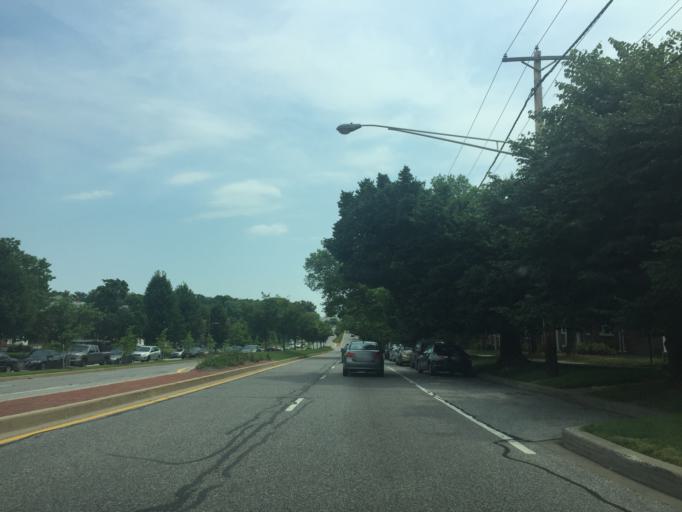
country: US
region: Maryland
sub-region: Baltimore County
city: Parkville
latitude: 39.3889
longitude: -76.5709
